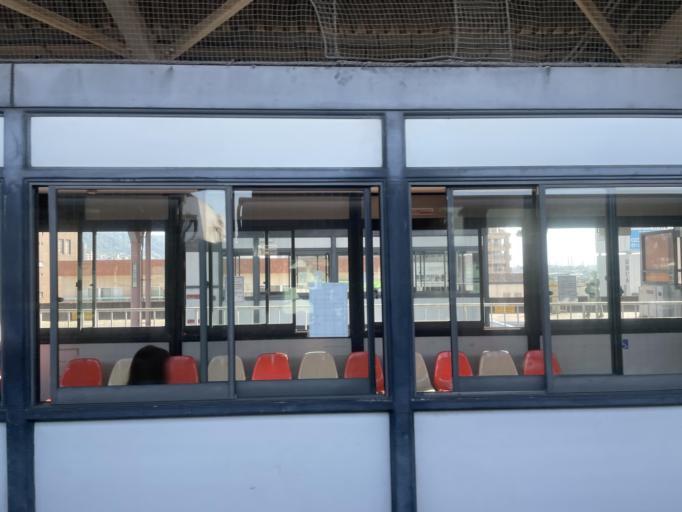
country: JP
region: Osaka
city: Daitocho
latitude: 34.6802
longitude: 135.6410
